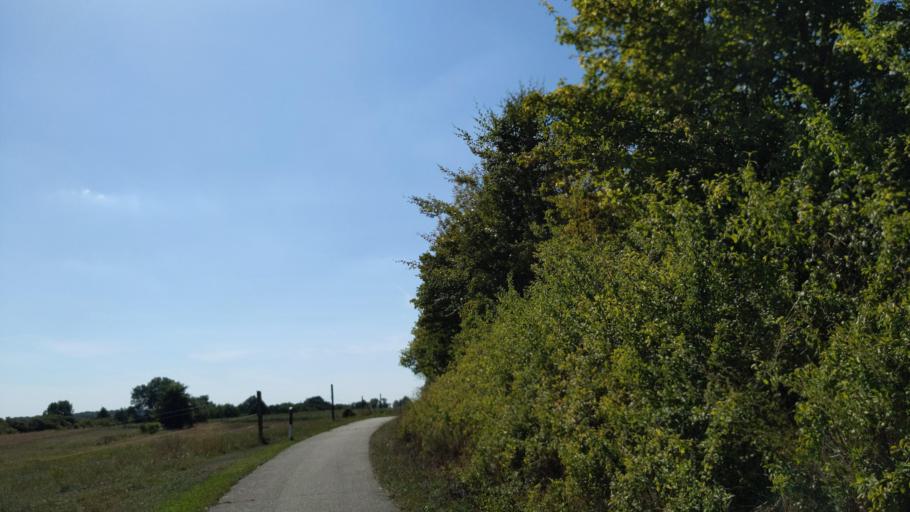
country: DE
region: Mecklenburg-Vorpommern
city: Selmsdorf
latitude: 53.8307
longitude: 10.8673
